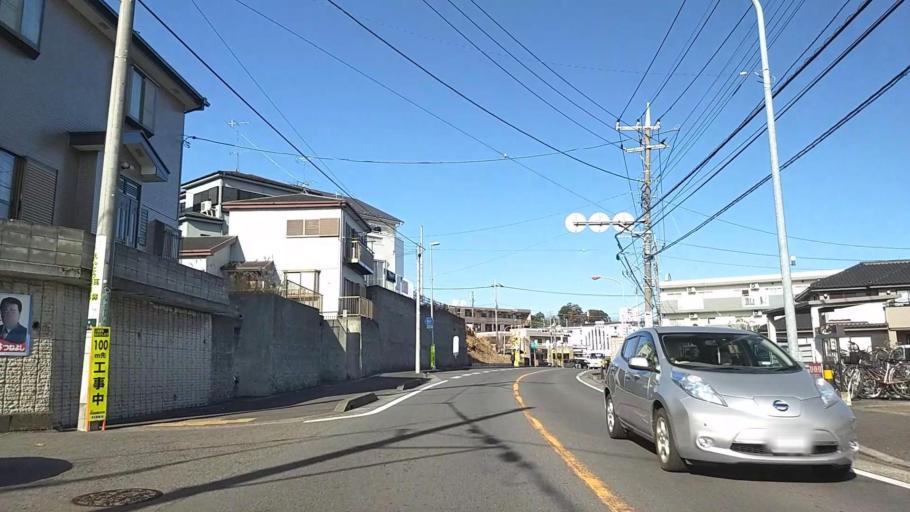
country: JP
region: Kanagawa
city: Atsugi
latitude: 35.4551
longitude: 139.3489
